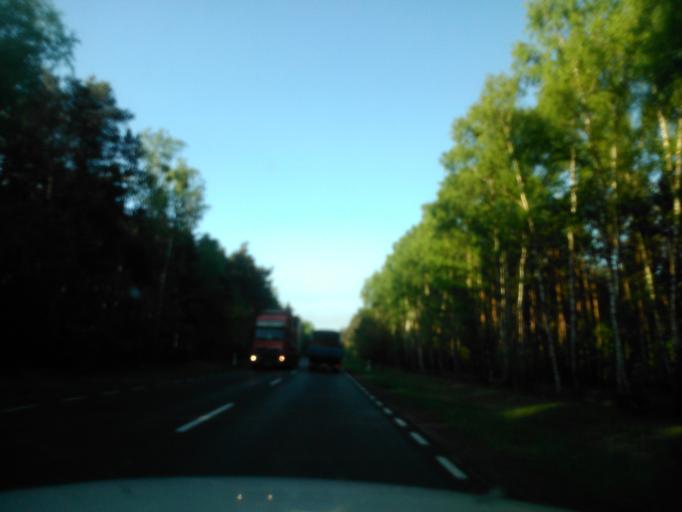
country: PL
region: Masovian Voivodeship
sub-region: Powiat sochaczewski
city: Mlodzieszyn
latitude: 52.3240
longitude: 20.2106
